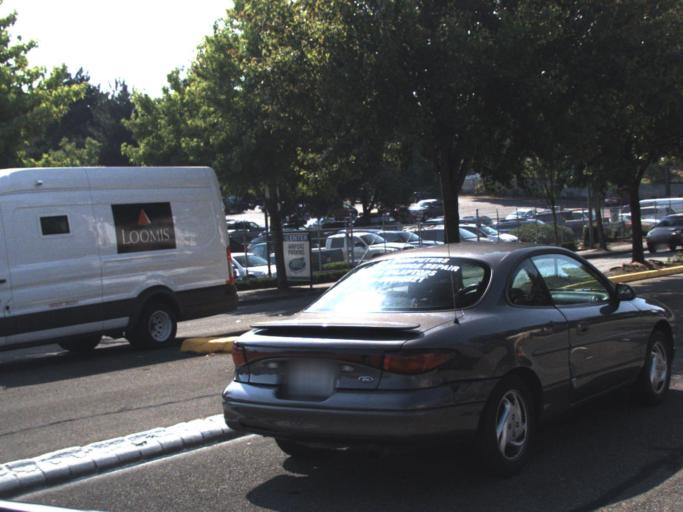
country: US
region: Washington
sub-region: King County
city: SeaTac
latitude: 47.4330
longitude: -122.2955
